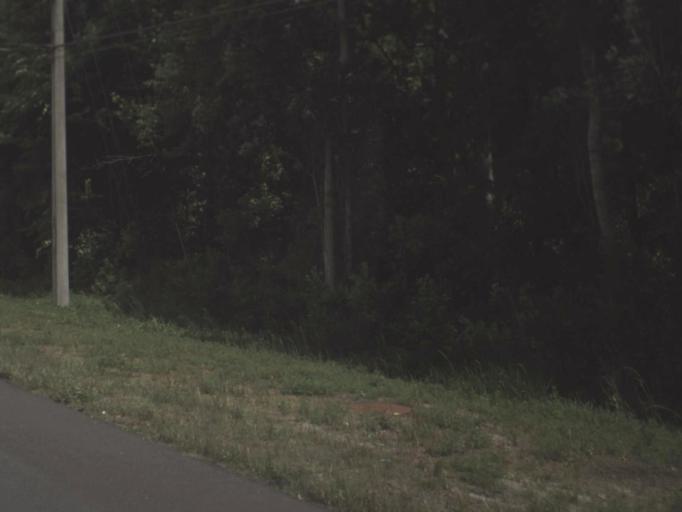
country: US
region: Florida
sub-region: Saint Johns County
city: Fruit Cove
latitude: 30.2117
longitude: -81.5805
